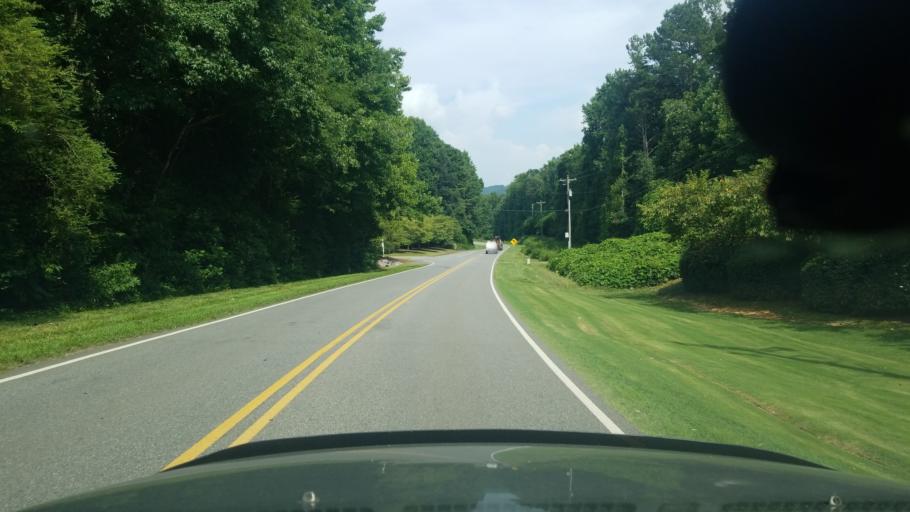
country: US
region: Georgia
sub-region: Dawson County
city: Dawsonville
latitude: 34.3132
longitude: -84.0753
